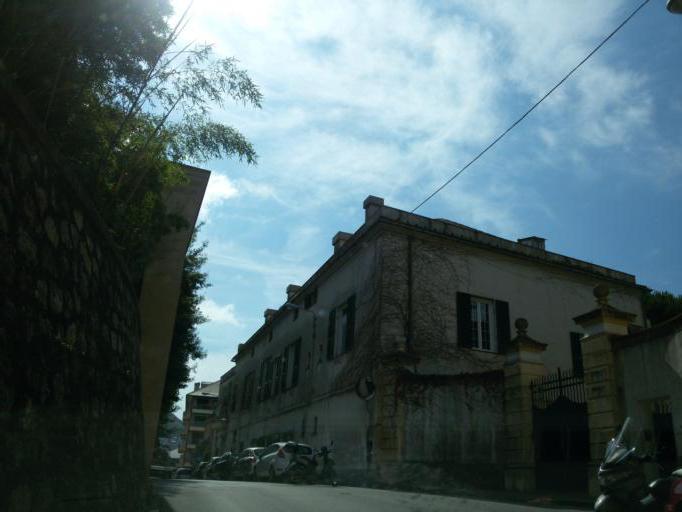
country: IT
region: Liguria
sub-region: Provincia di Genova
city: Bogliasco
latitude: 44.3973
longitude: 8.9958
